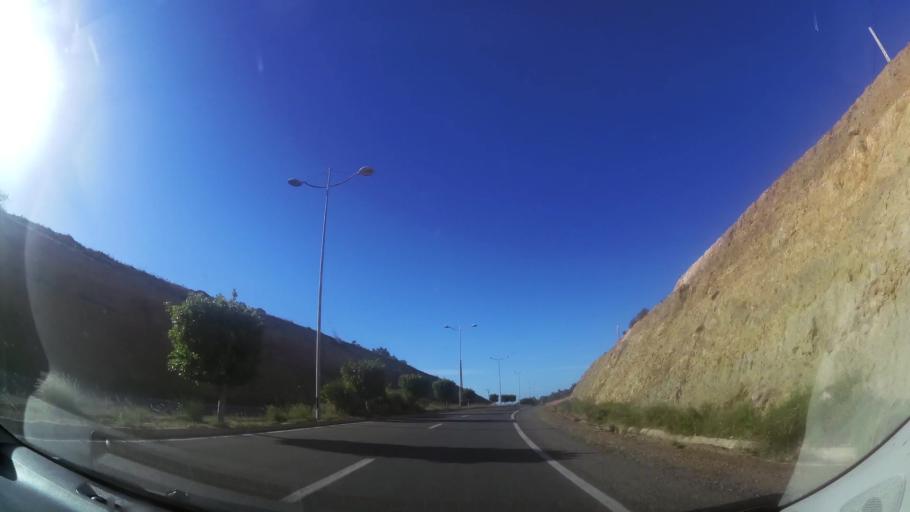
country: MA
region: Oriental
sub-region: Berkane-Taourirt
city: Madagh
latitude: 35.0552
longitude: -2.2222
